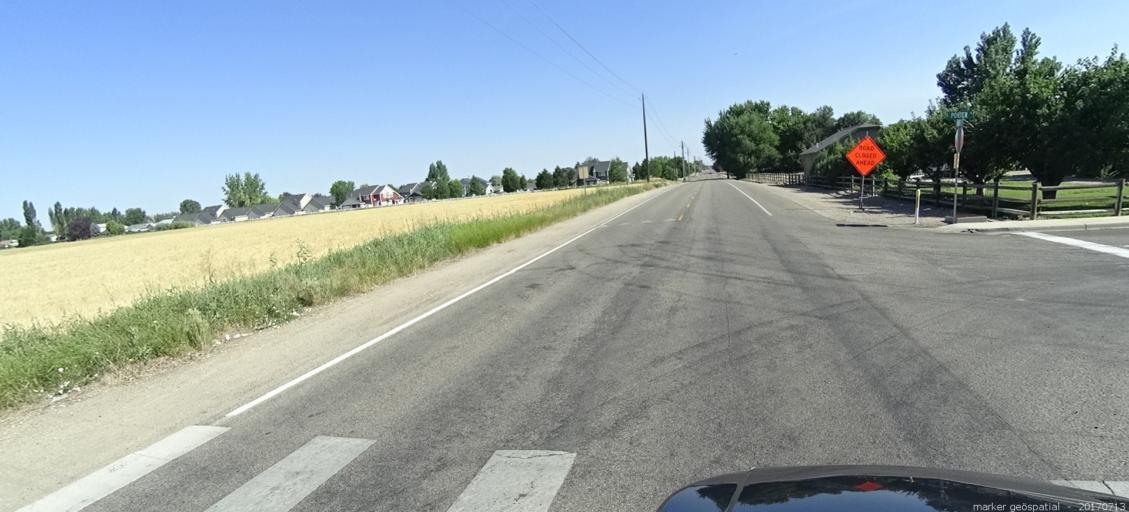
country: US
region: Idaho
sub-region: Ada County
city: Kuna
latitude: 43.4980
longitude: -116.4137
